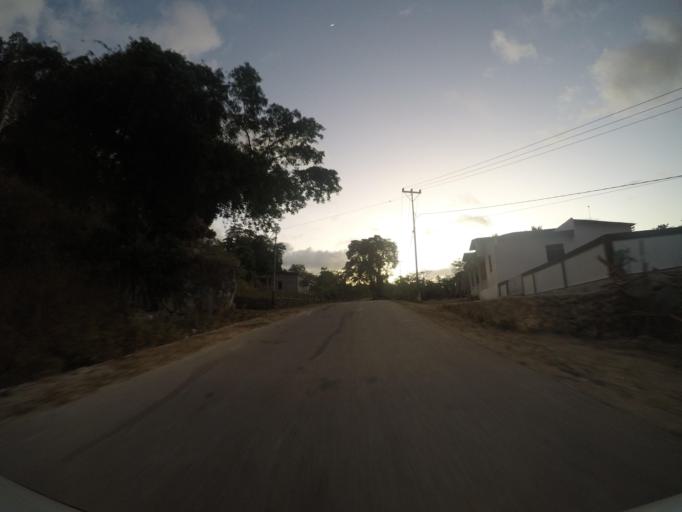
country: TL
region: Lautem
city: Lospalos
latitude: -8.3715
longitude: 127.0289
